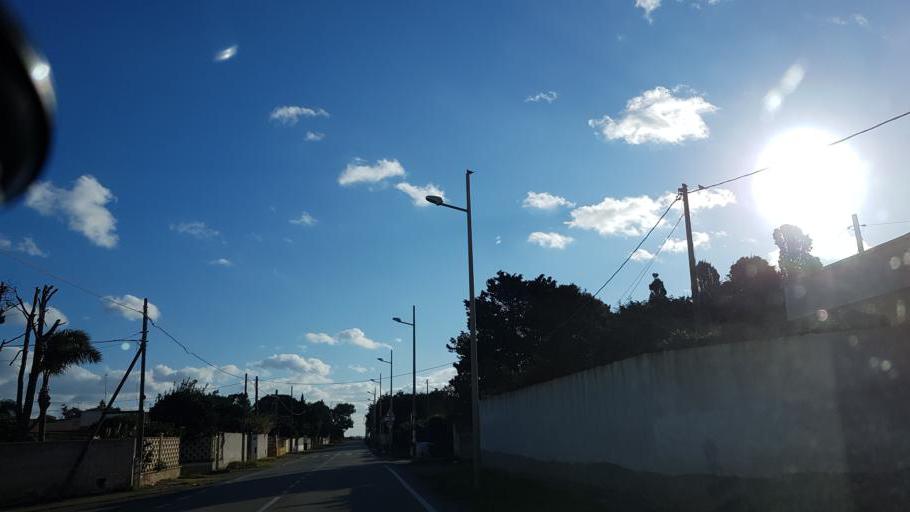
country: IT
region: Apulia
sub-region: Provincia di Brindisi
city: Materdomini
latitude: 40.6790
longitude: 17.9354
